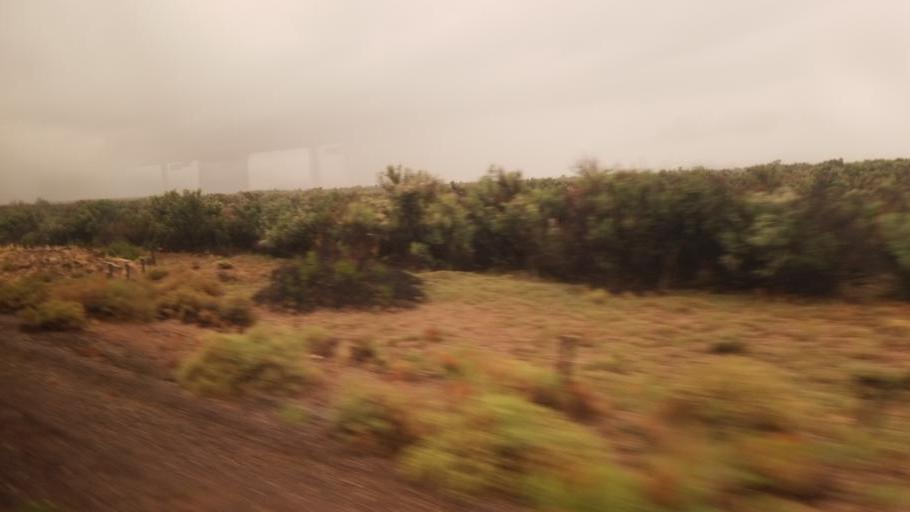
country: US
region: Arizona
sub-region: Navajo County
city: Joseph City
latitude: 34.9674
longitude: -110.4595
